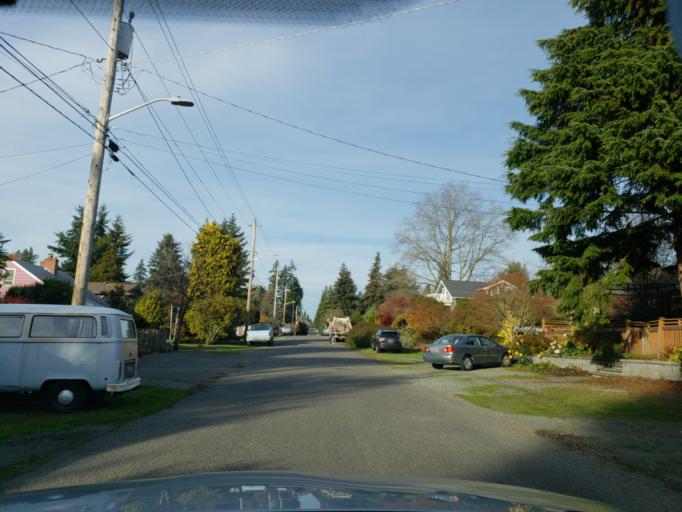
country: US
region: Washington
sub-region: King County
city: Shoreline
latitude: 47.7090
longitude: -122.3582
